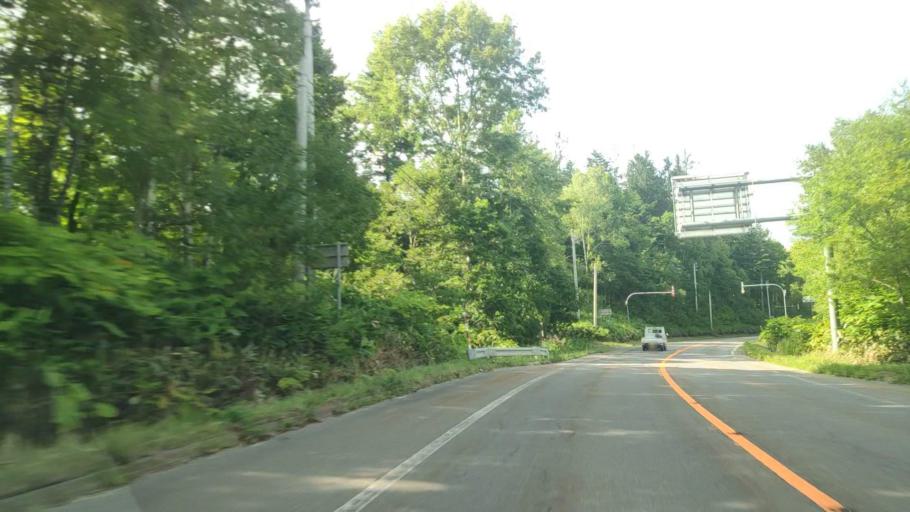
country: JP
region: Hokkaido
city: Nayoro
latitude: 44.3870
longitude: 142.3980
